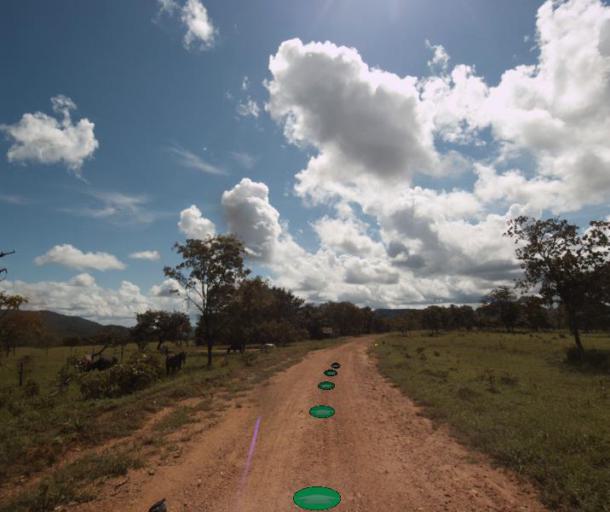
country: BR
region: Goias
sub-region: Pirenopolis
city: Pirenopolis
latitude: -15.7829
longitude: -48.9349
